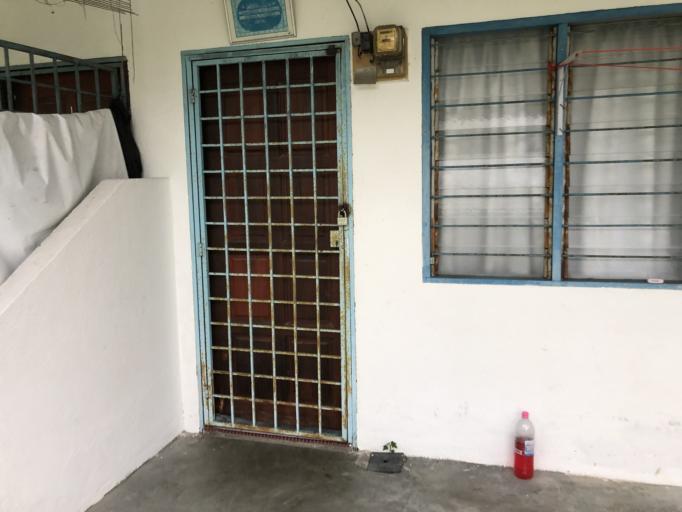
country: MY
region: Selangor
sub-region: Petaling
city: Petaling Jaya
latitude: 3.1704
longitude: 101.6267
